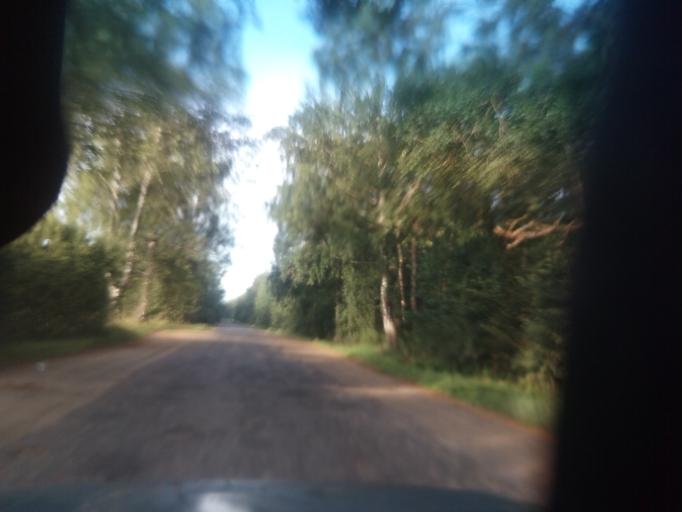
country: BY
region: Vitebsk
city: Dzisna
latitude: 55.6343
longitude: 28.3053
